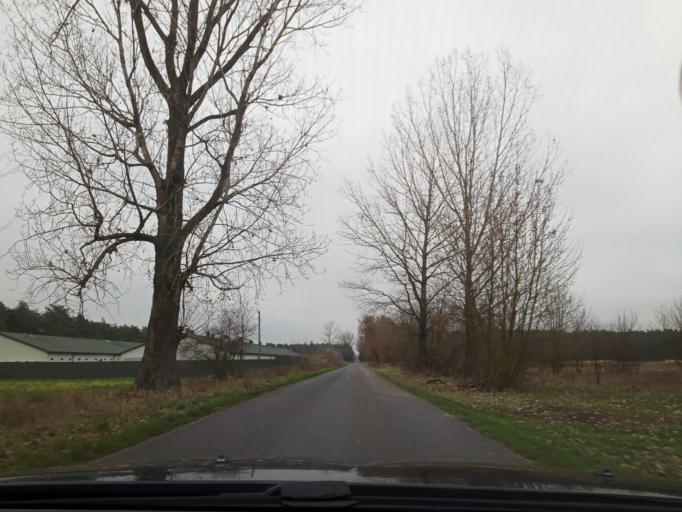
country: PL
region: Swietokrzyskie
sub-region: Powiat jedrzejowski
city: Imielno
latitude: 50.5853
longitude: 20.4593
